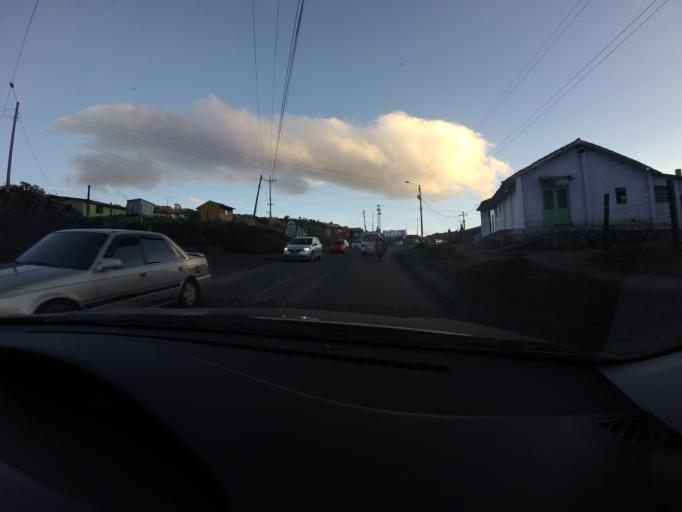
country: CO
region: Cundinamarca
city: Sutatausa
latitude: 5.1868
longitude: -73.8796
